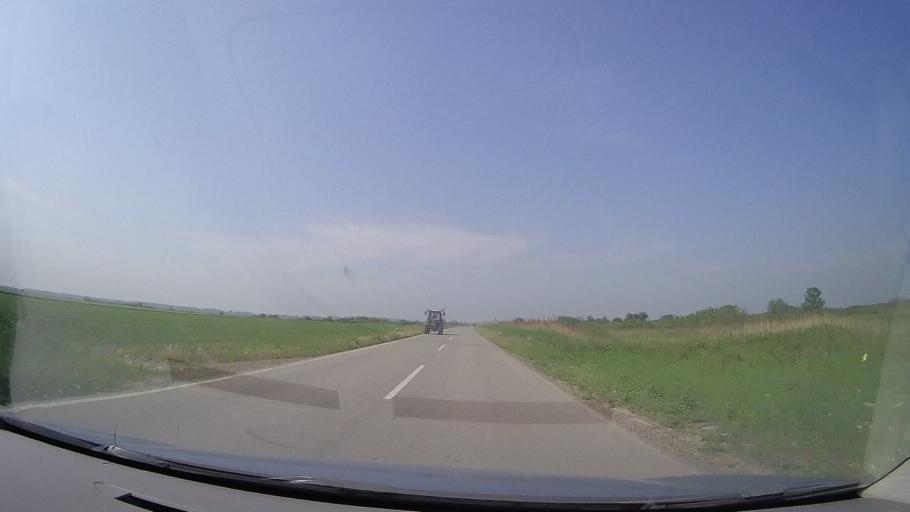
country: RS
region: Autonomna Pokrajina Vojvodina
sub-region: Srednjebanatski Okrug
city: Secanj
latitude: 45.3903
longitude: 20.8023
